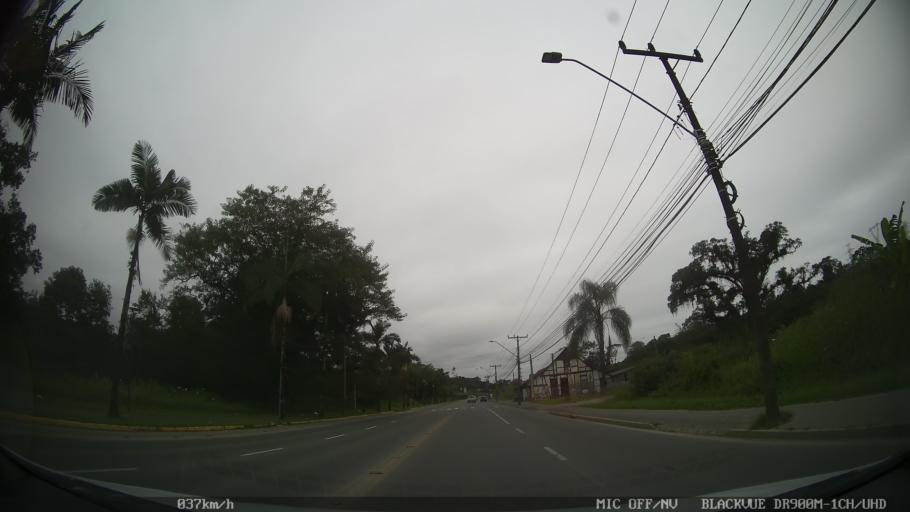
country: BR
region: Santa Catarina
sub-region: Joinville
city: Joinville
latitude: -26.2909
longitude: -48.8911
